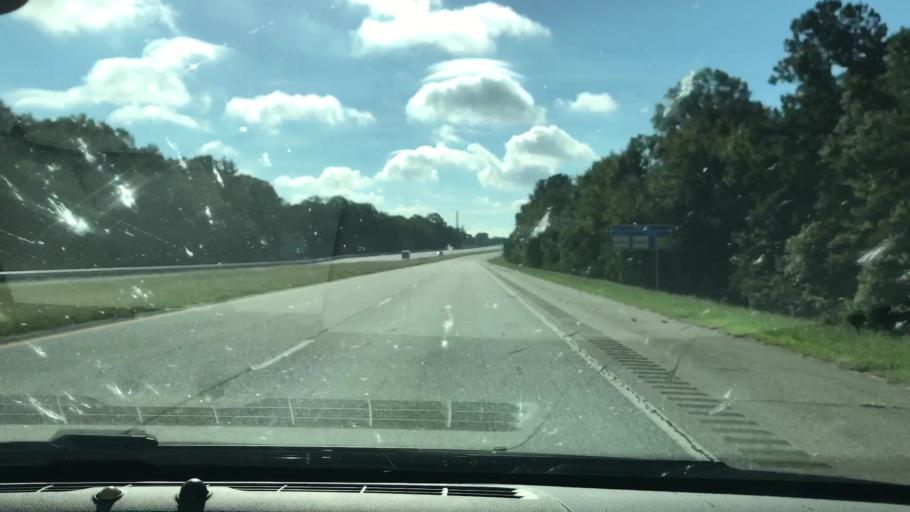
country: US
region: Georgia
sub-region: Dougherty County
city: Albany
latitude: 31.6117
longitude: -84.1639
